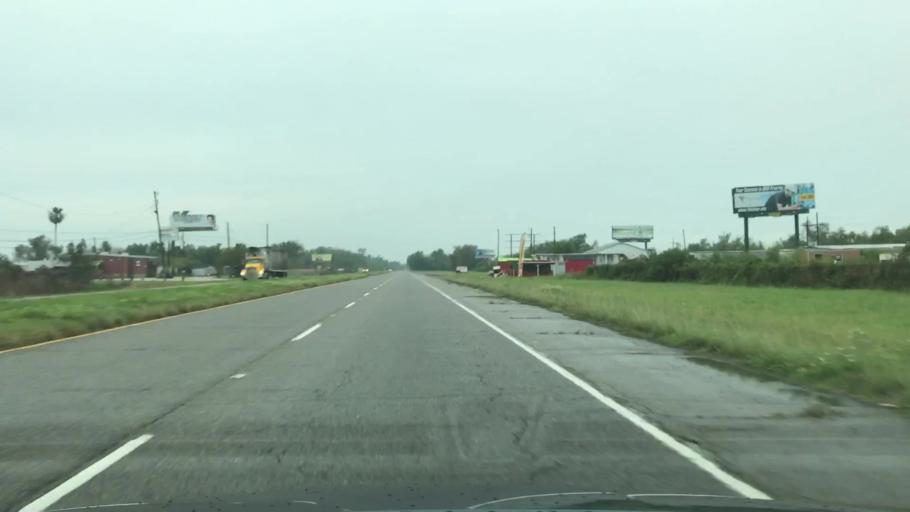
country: US
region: Louisiana
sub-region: Saint Charles Parish
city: Des Allemands
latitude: 29.8047
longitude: -90.4990
